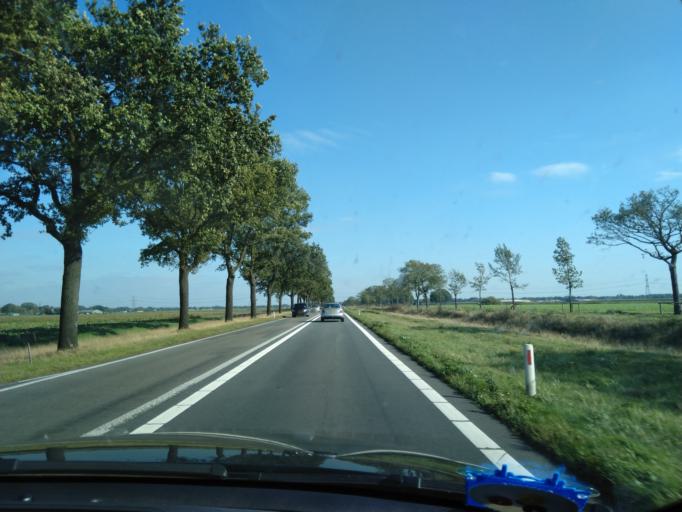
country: NL
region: Groningen
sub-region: Gemeente Veendam
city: Veendam
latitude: 53.0914
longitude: 6.9283
